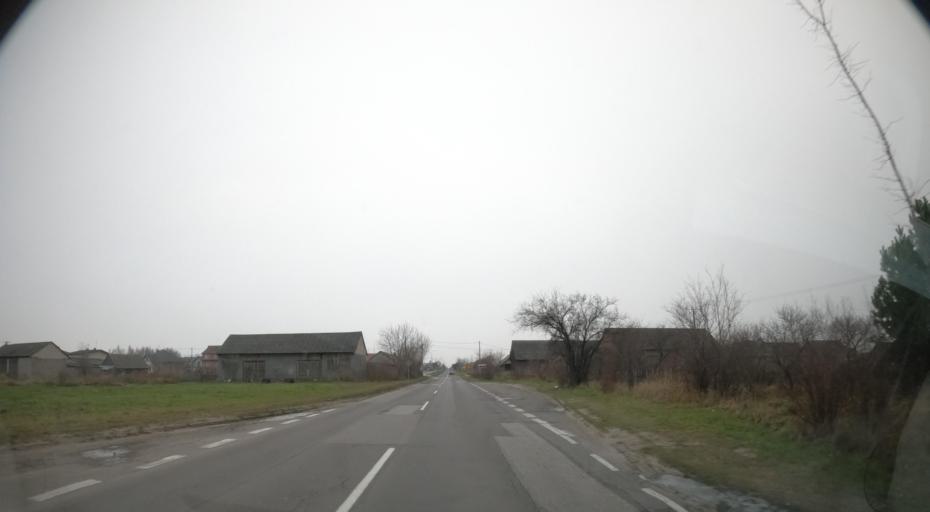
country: PL
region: Masovian Voivodeship
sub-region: Powiat radomski
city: Jastrzebia
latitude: 51.4505
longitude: 21.1940
